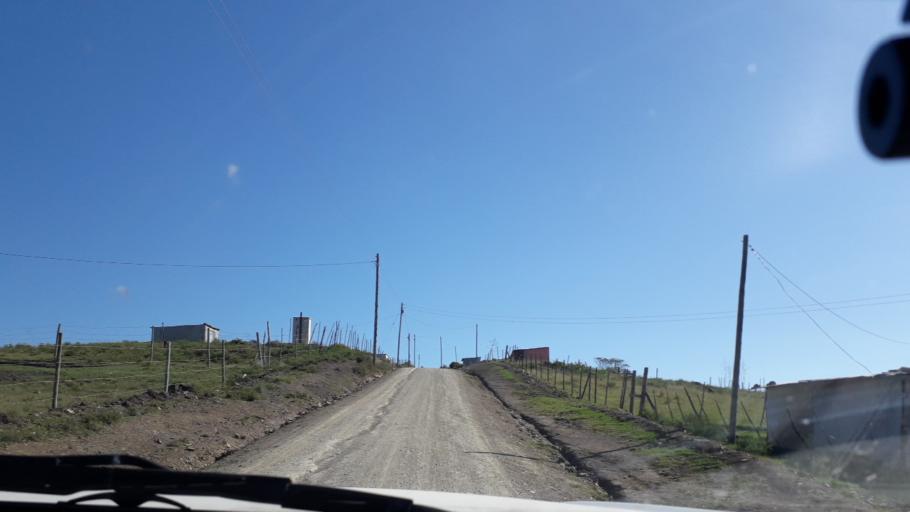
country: ZA
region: Eastern Cape
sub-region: Buffalo City Metropolitan Municipality
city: East London
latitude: -32.8001
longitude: 27.9664
